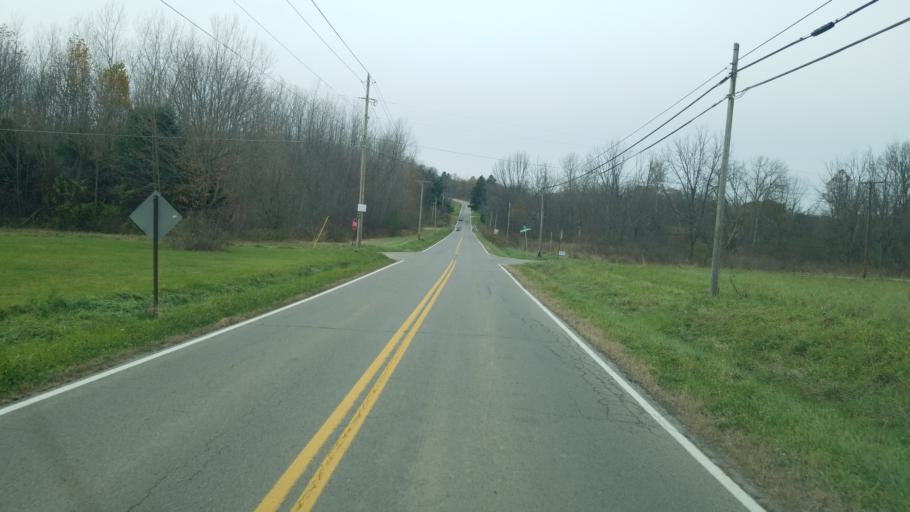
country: US
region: Ohio
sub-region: Richland County
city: Lincoln Heights
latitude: 40.7283
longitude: -82.4812
